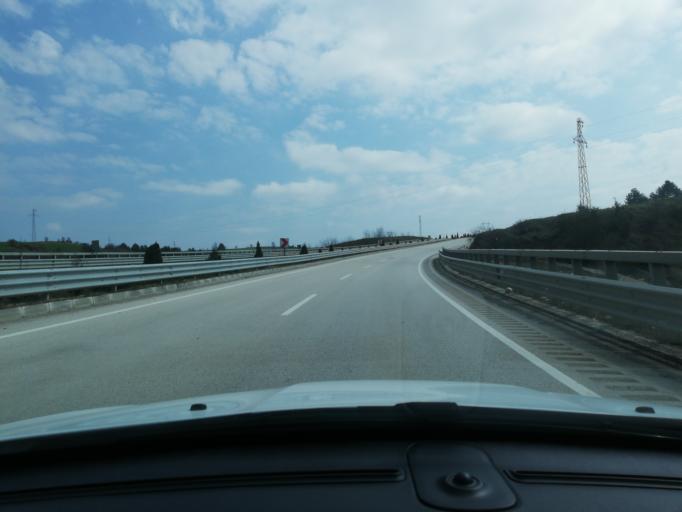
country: TR
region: Kastamonu
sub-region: Cide
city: Kastamonu
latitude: 41.3748
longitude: 33.7924
